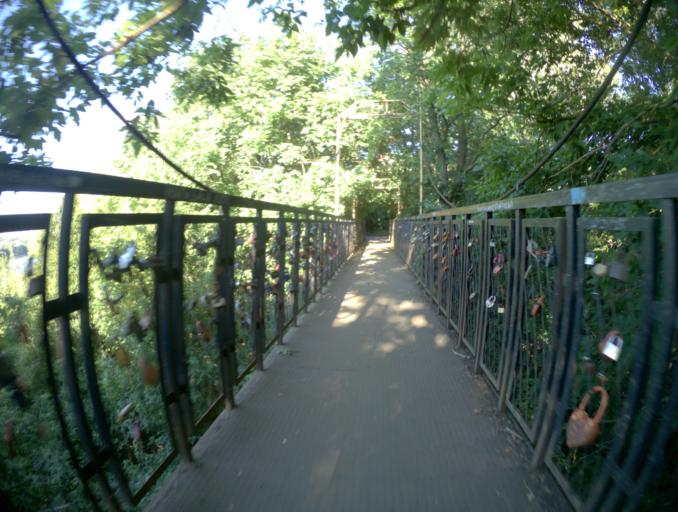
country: RU
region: Nizjnij Novgorod
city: Pavlovo
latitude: 55.9651
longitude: 43.0574
